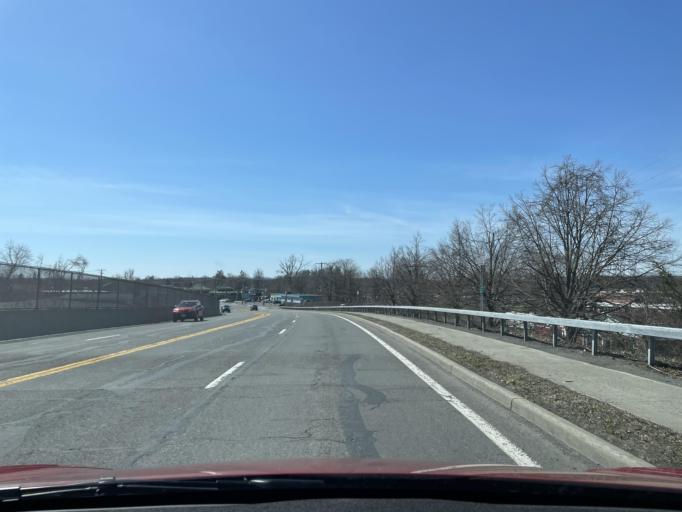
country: US
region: New York
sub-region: Ulster County
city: Lincoln Park
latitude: 41.9587
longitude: -73.9928
